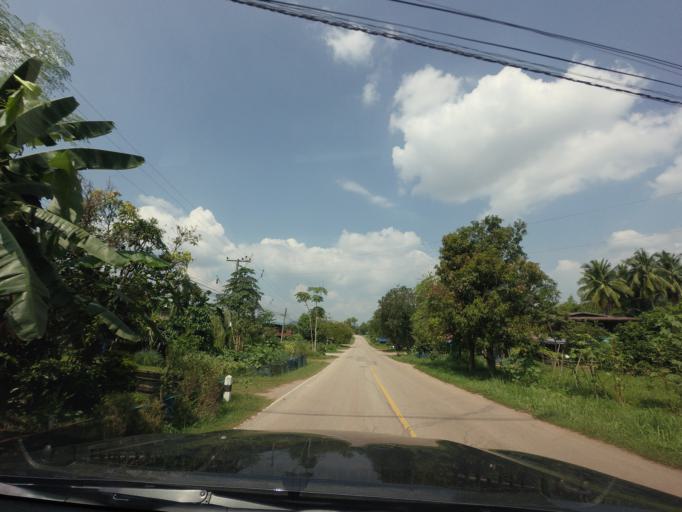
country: TH
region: Uttaradit
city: Ban Khok
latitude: 18.0062
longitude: 101.0367
